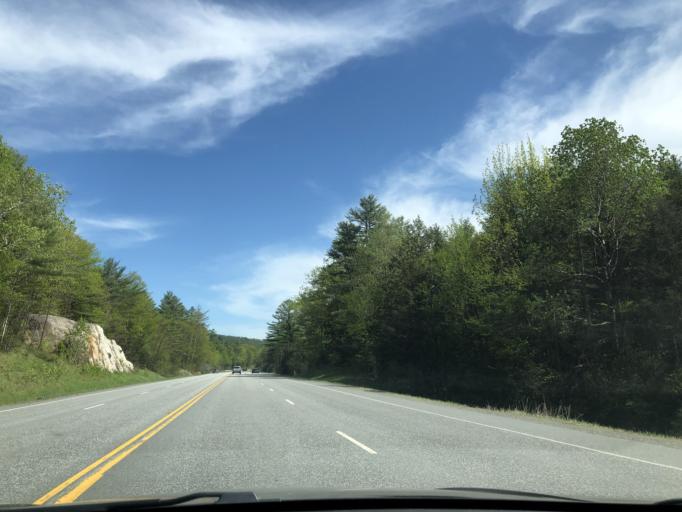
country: US
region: New Hampshire
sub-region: Grafton County
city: Lebanon
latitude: 43.6694
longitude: -72.2538
